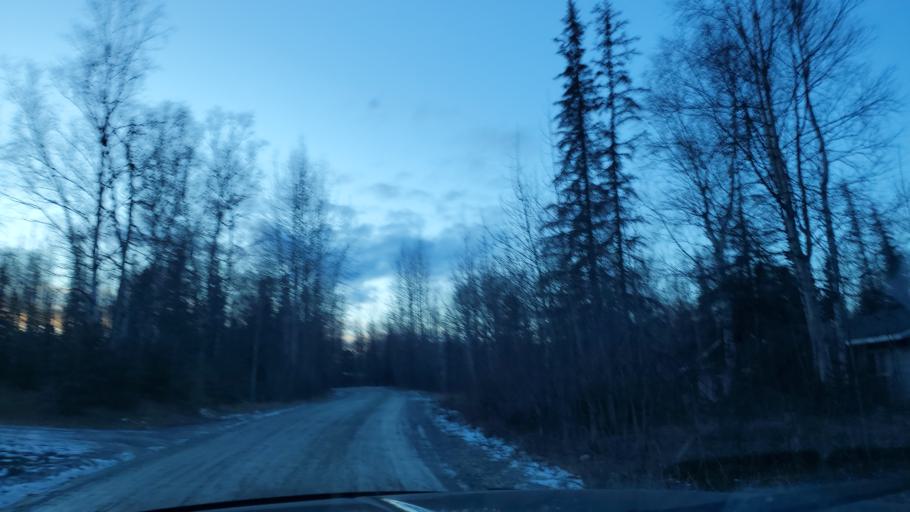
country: US
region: Alaska
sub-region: Matanuska-Susitna Borough
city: Tanaina
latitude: 61.6129
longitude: -149.4019
